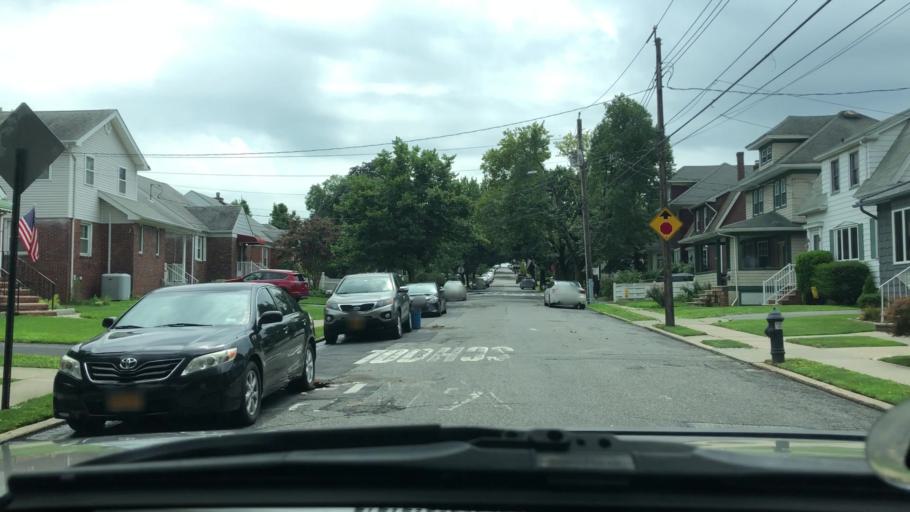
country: US
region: New Jersey
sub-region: Hudson County
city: Bayonne
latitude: 40.6282
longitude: -74.1097
